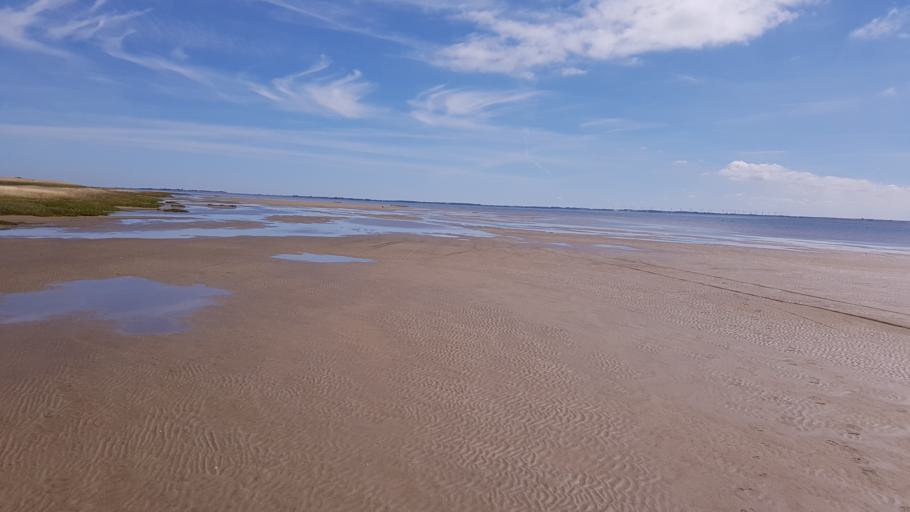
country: DE
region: Schleswig-Holstein
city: List
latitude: 55.0748
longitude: 8.5414
